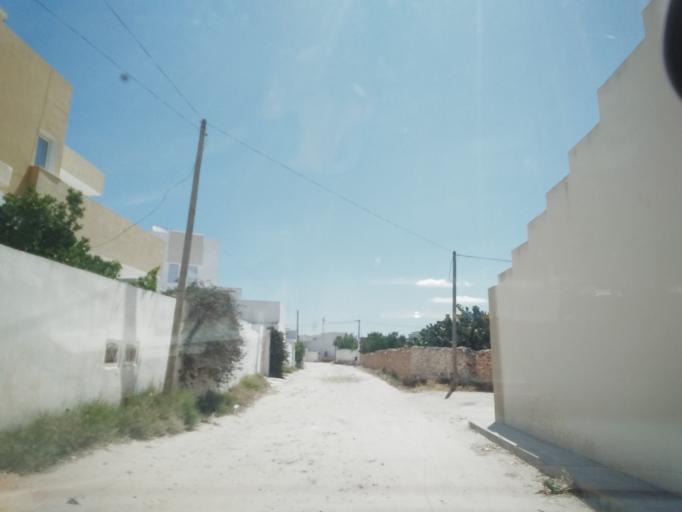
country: TN
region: Safaqis
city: Al Qarmadah
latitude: 34.8218
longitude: 10.7637
